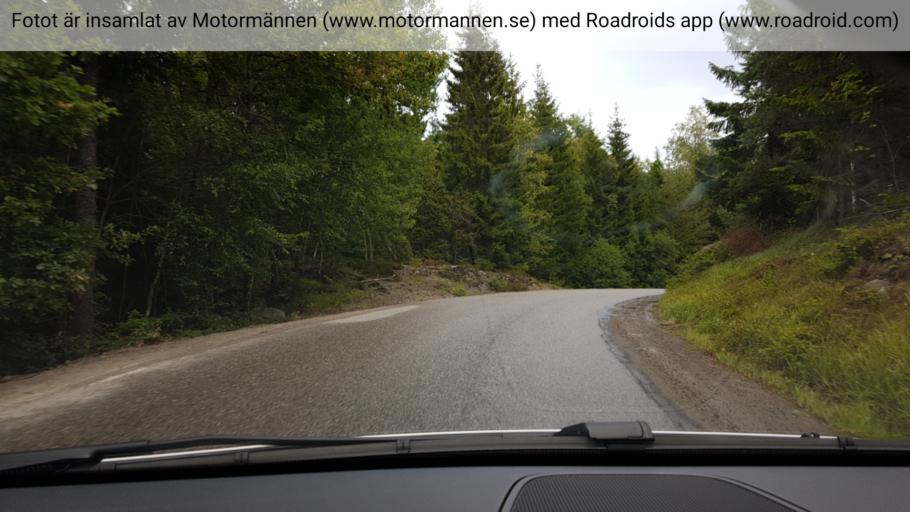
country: SE
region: Stockholm
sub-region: Nynashamns Kommun
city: Osmo
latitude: 59.0415
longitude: 17.9126
